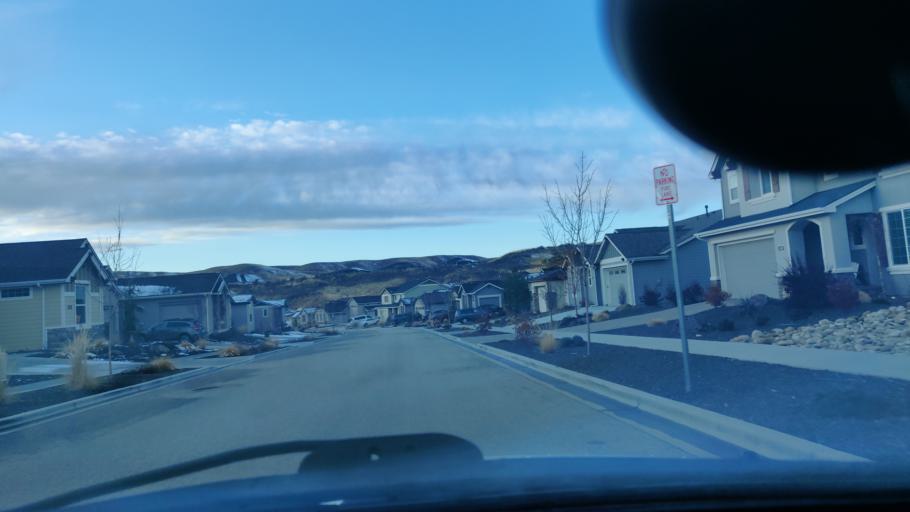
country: US
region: Idaho
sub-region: Ada County
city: Eagle
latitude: 43.7738
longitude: -116.2554
